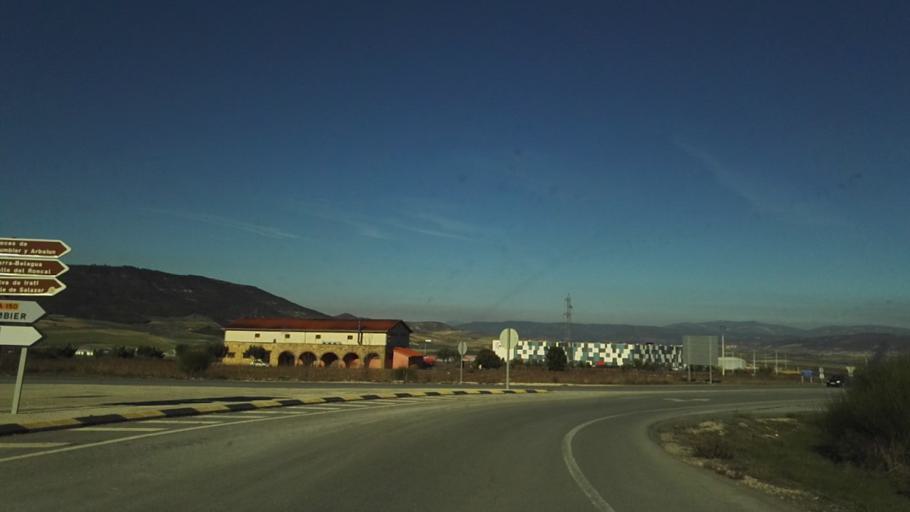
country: ES
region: Navarre
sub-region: Provincia de Navarra
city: Lumbier
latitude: 42.6418
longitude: -1.3379
